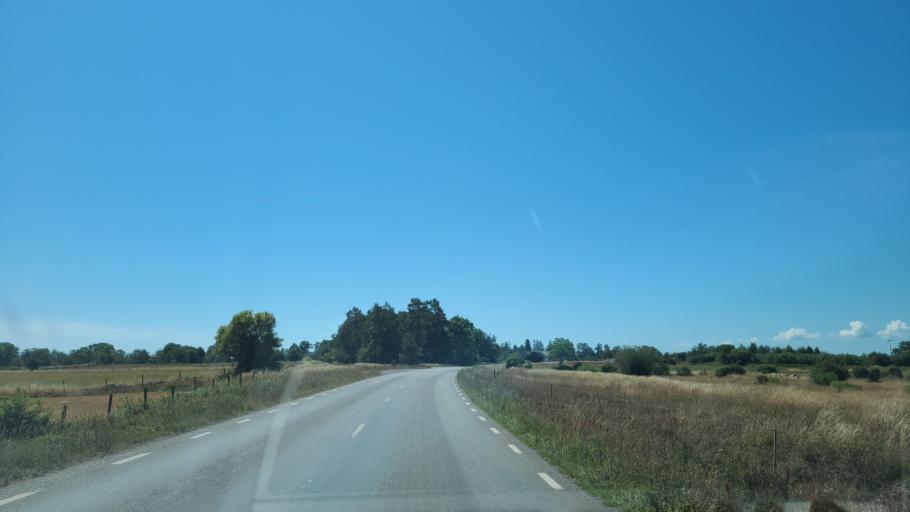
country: SE
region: Kalmar
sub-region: Borgholms Kommun
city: Borgholm
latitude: 56.7323
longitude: 16.7222
